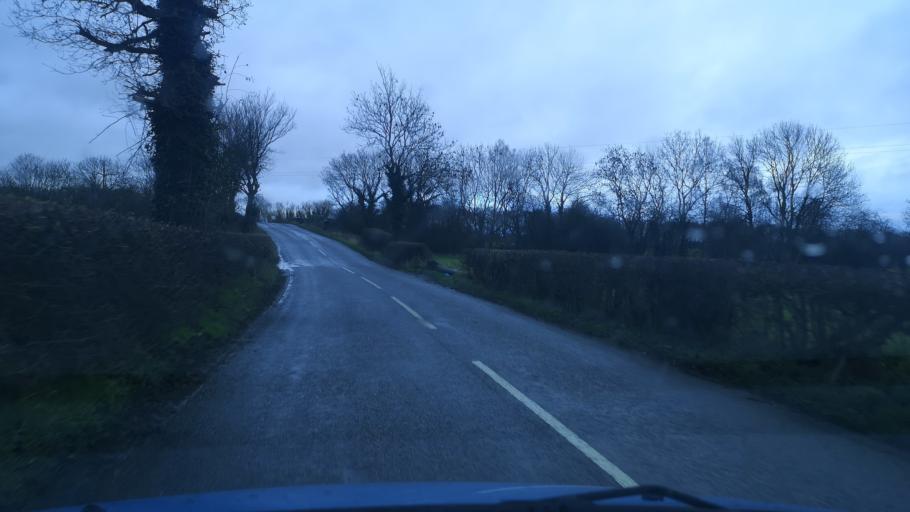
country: GB
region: England
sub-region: City and Borough of Wakefield
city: Ryhill
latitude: 53.6365
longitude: -1.4159
